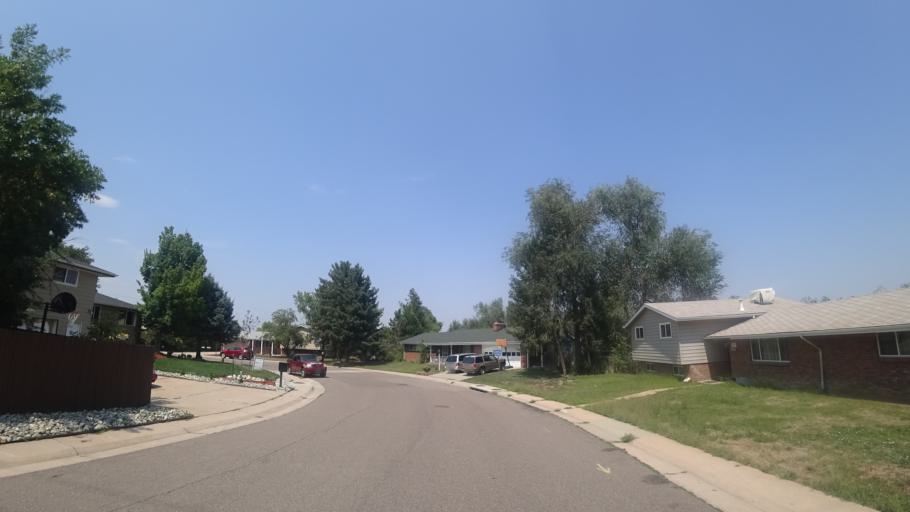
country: US
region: Colorado
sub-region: Arapahoe County
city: Greenwood Village
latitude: 39.6117
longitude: -104.9813
